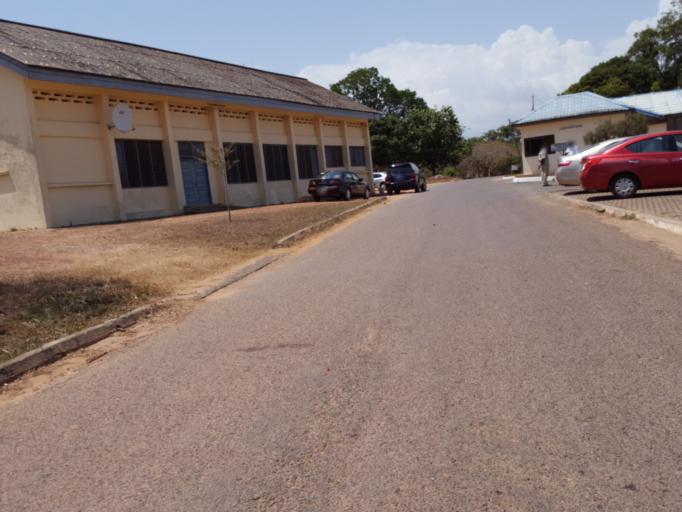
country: GH
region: Central
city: Cape Coast
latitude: 5.1207
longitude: -1.2901
